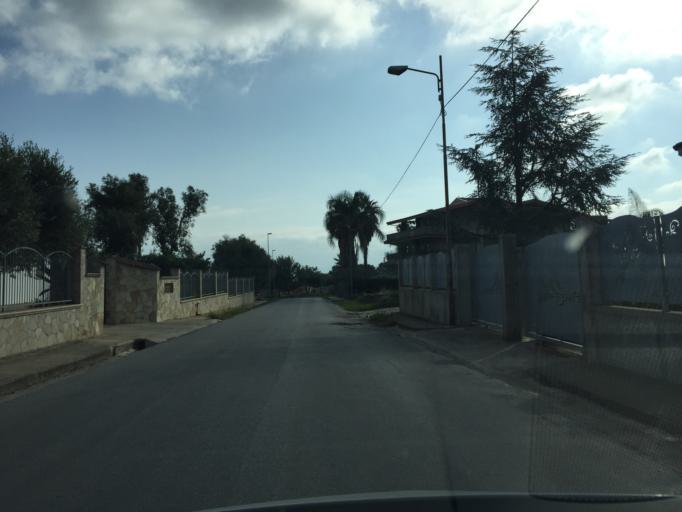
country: IT
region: Calabria
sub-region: Provincia di Vibo-Valentia
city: Pannaconi
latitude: 38.7029
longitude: 16.0464
